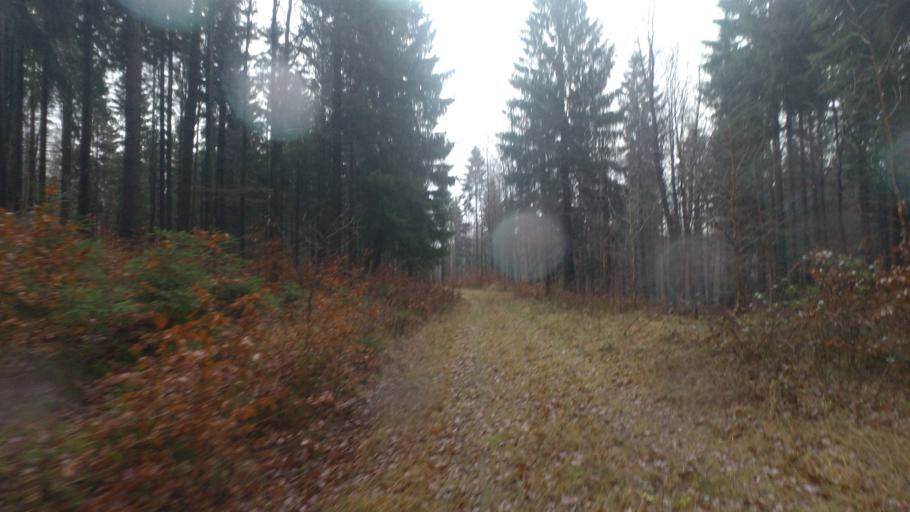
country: DE
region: Thuringia
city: Frankenhain
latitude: 50.7238
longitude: 10.7886
